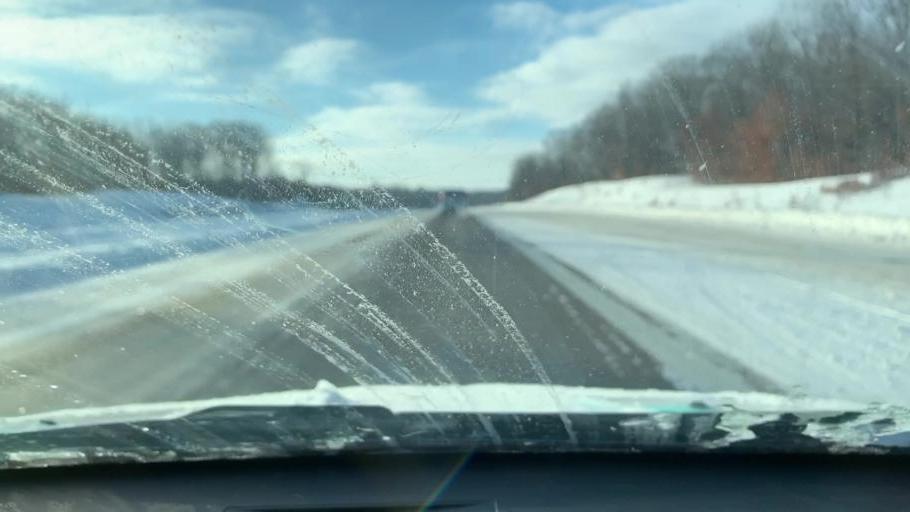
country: US
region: Michigan
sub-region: Wexford County
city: Cadillac
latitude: 44.2475
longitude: -85.3684
